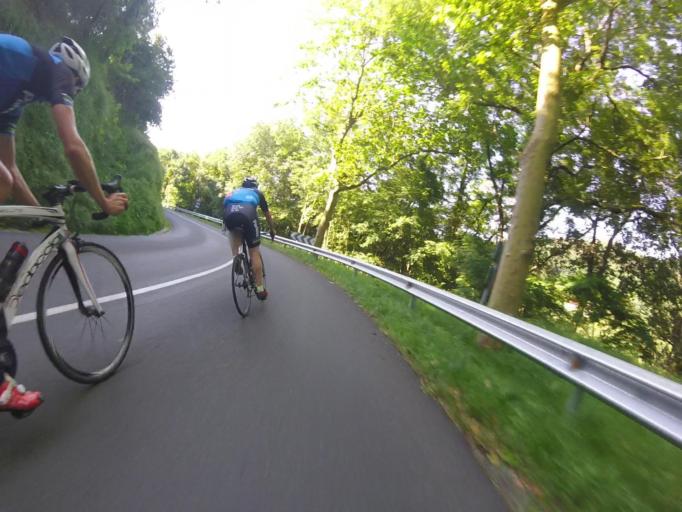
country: ES
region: Basque Country
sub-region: Provincia de Guipuzcoa
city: Asteasu
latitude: 43.2055
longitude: -2.1122
